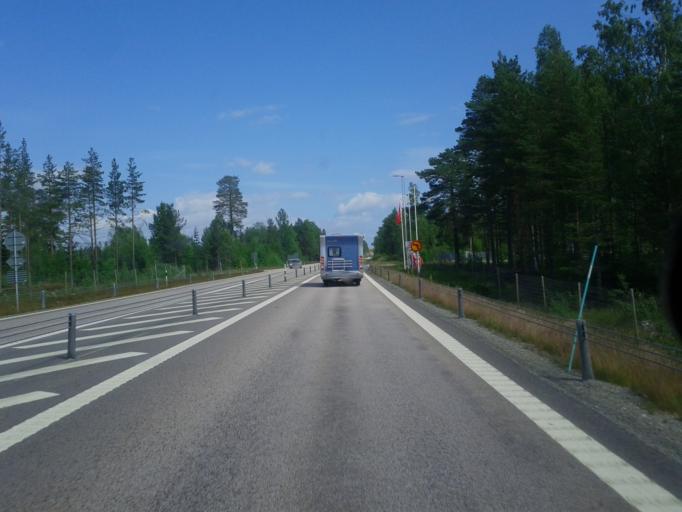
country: SE
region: Vaesternorrland
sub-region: OErnskoeldsviks Kommun
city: Husum
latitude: 63.4799
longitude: 19.2948
